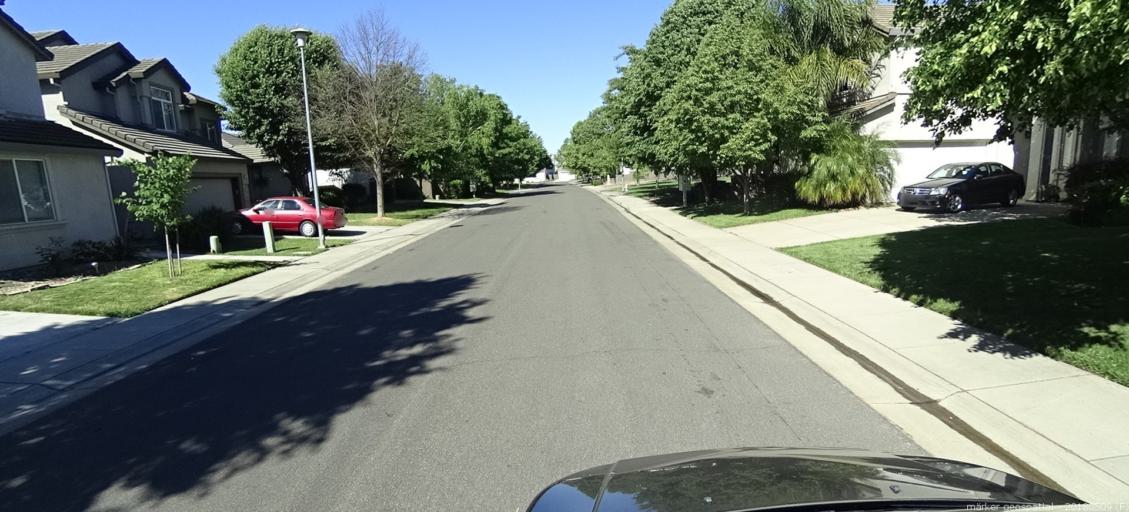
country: US
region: California
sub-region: Sacramento County
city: Elverta
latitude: 38.6711
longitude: -121.5199
